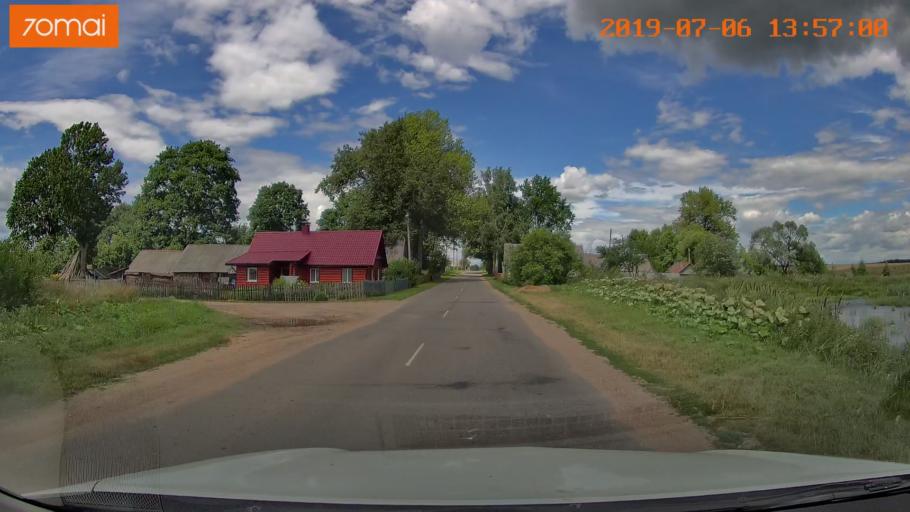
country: BY
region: Minsk
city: Ivyanyets
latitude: 53.7704
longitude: 26.8054
